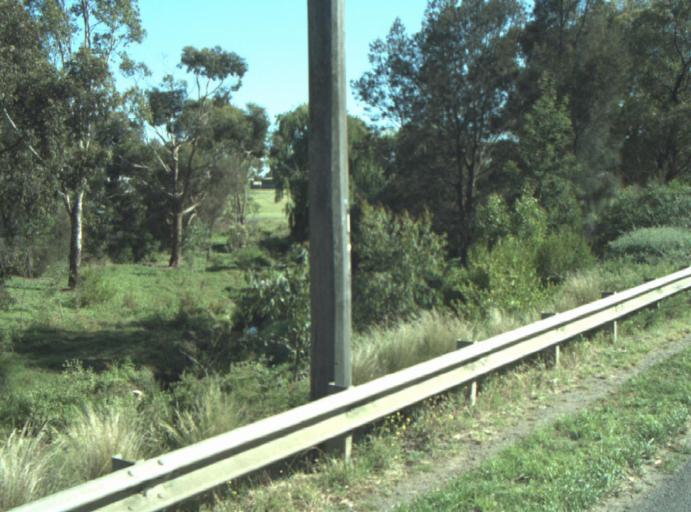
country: AU
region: Victoria
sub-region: Greater Geelong
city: Bell Park
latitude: -38.0991
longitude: 144.3502
